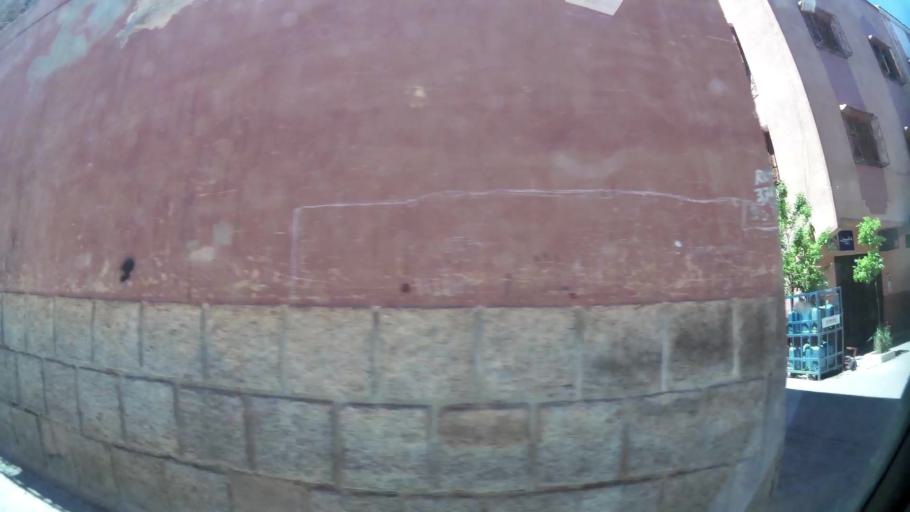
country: MA
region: Marrakech-Tensift-Al Haouz
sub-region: Marrakech
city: Marrakesh
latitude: 31.6486
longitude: -7.9941
